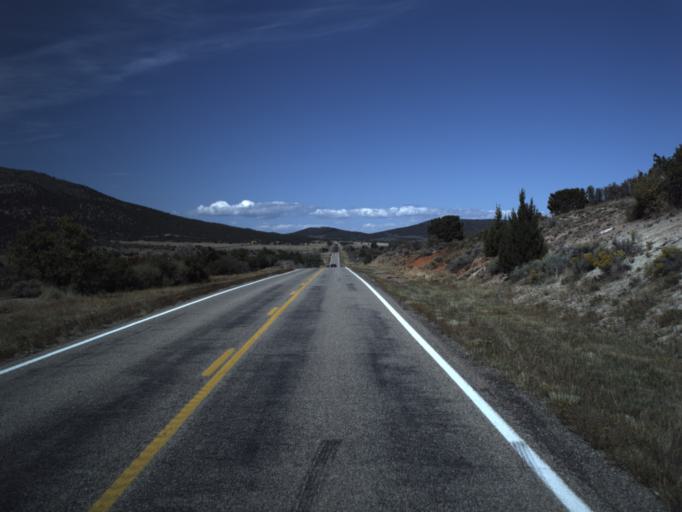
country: US
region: Utah
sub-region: Washington County
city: Enterprise
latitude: 37.4814
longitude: -113.6286
